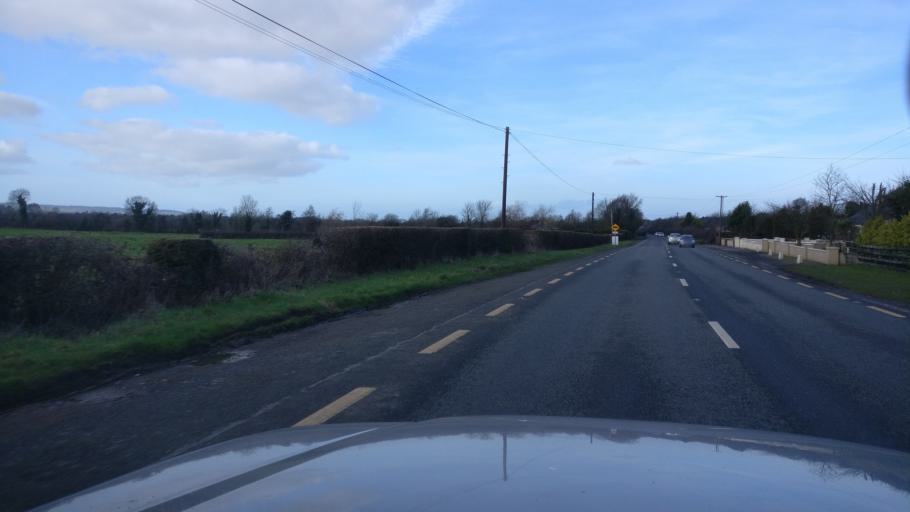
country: IE
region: Leinster
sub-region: Laois
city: Portlaoise
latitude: 53.0592
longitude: -7.3243
